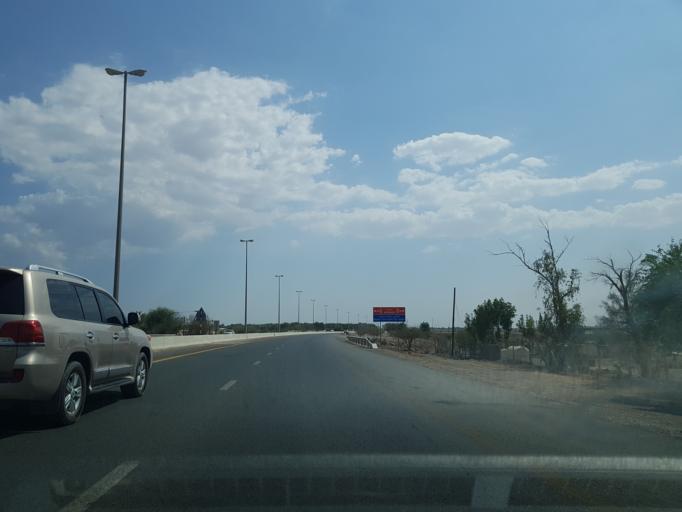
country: AE
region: Ash Shariqah
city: Adh Dhayd
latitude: 25.2404
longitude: 55.9154
